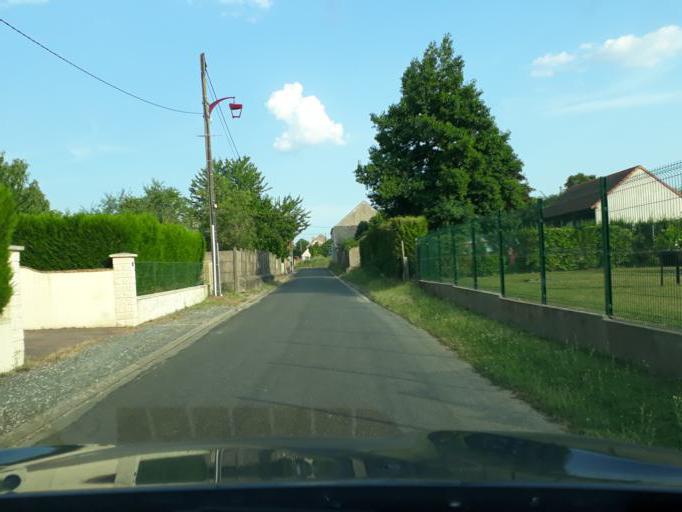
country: FR
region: Centre
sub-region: Departement du Loir-et-Cher
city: Mer
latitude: 47.8020
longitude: 1.4901
